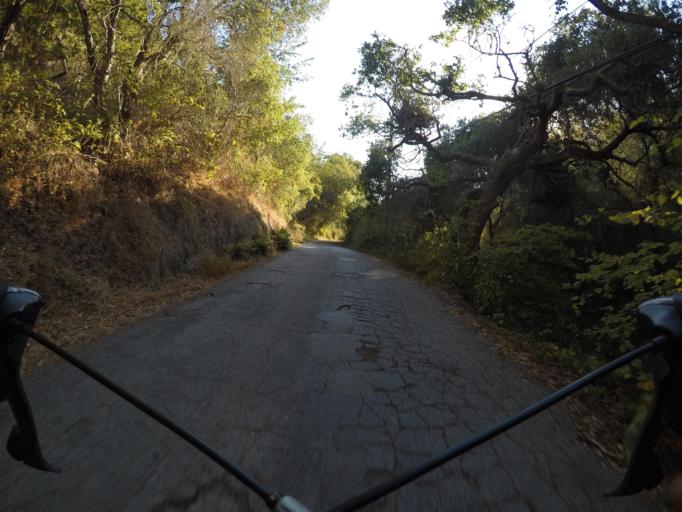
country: US
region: California
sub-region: Santa Cruz County
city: Live Oak
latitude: 37.0001
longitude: -121.9857
